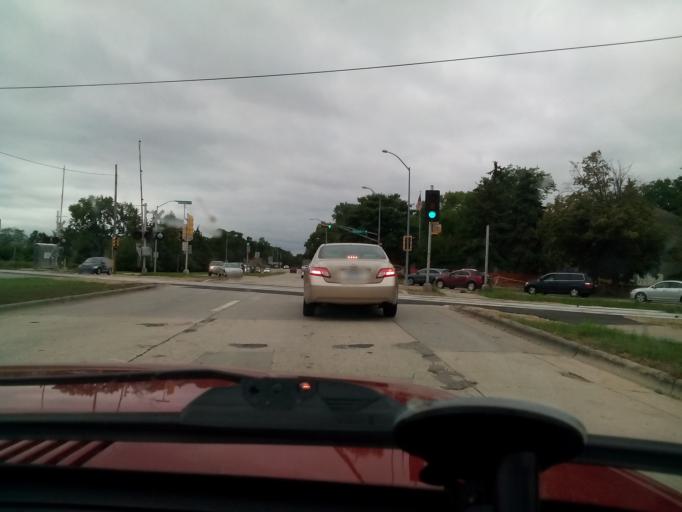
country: US
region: Wisconsin
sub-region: Dane County
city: Maple Bluff
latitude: 43.0937
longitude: -89.3631
